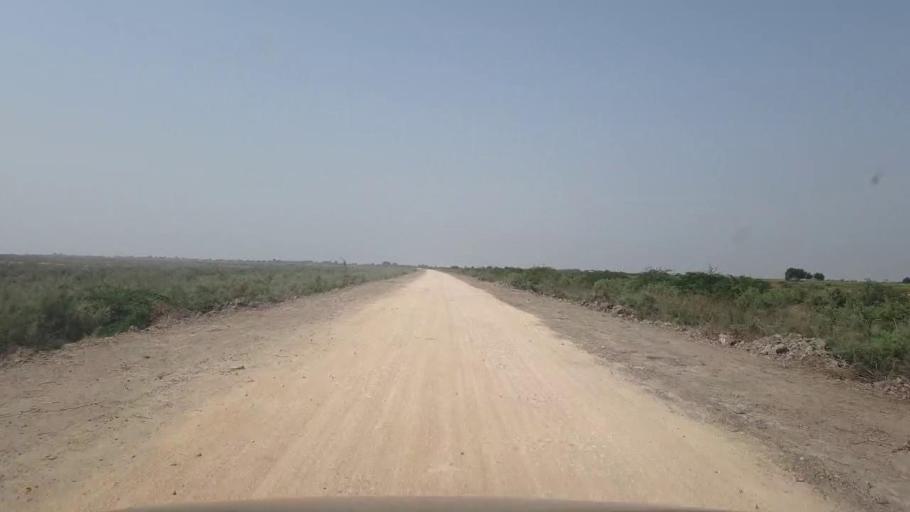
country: PK
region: Sindh
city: Jati
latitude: 24.3741
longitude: 68.5698
